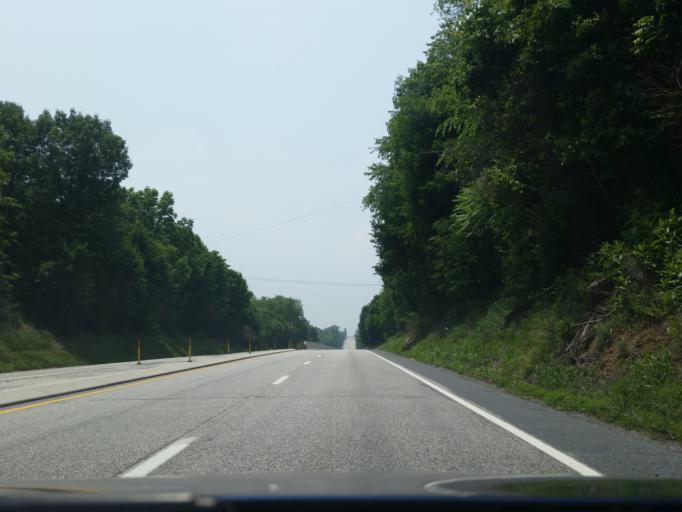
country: US
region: Pennsylvania
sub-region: Lebanon County
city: Palmyra
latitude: 40.3864
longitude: -76.6254
